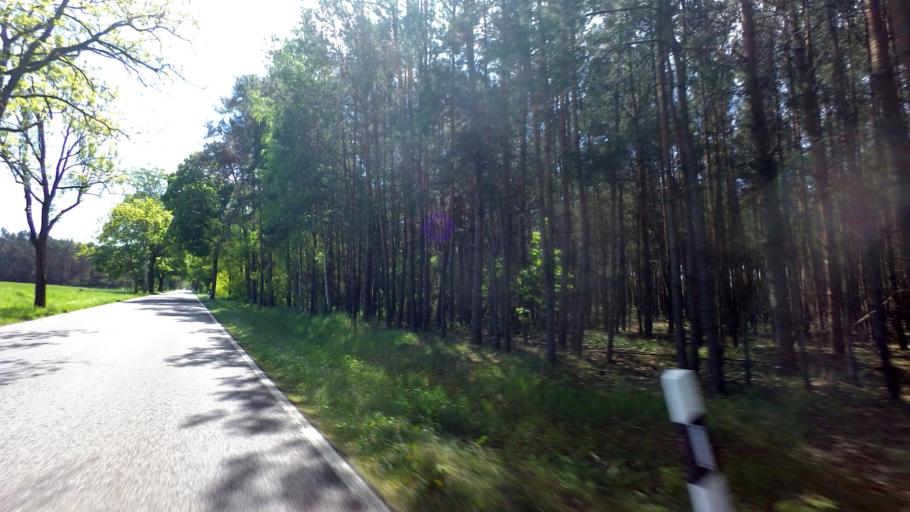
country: DE
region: Brandenburg
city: Luckenwalde
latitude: 52.1505
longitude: 13.1096
